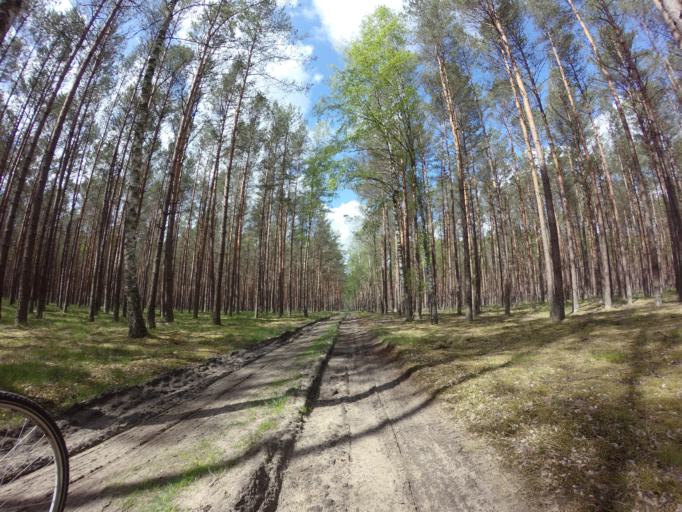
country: PL
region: West Pomeranian Voivodeship
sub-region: Powiat drawski
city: Kalisz Pomorski
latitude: 53.1938
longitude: 15.9920
